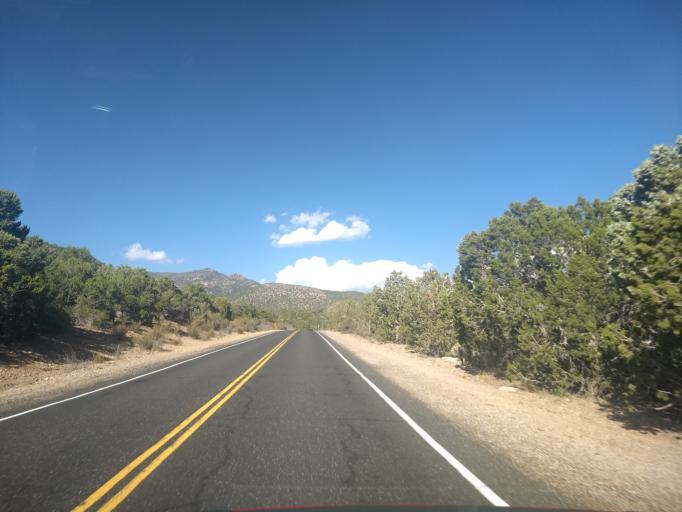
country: US
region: Utah
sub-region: Washington County
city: Enterprise
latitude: 37.4177
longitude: -113.5979
